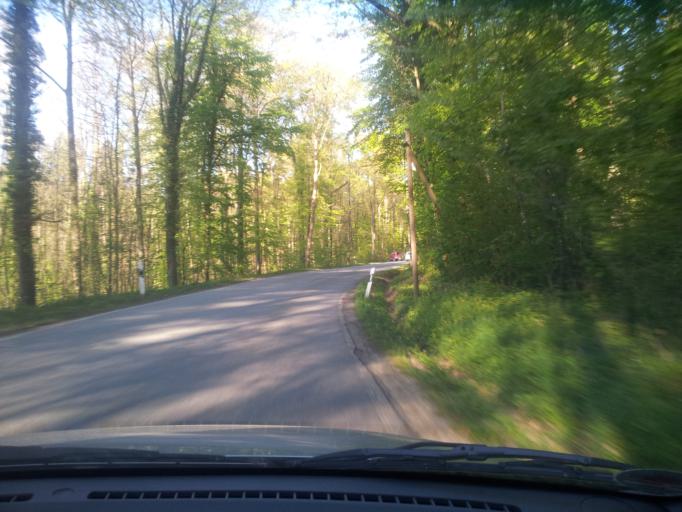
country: DE
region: Baden-Wuerttemberg
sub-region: Regierungsbezirk Stuttgart
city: Ilsfeld
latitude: 49.0417
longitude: 9.2433
